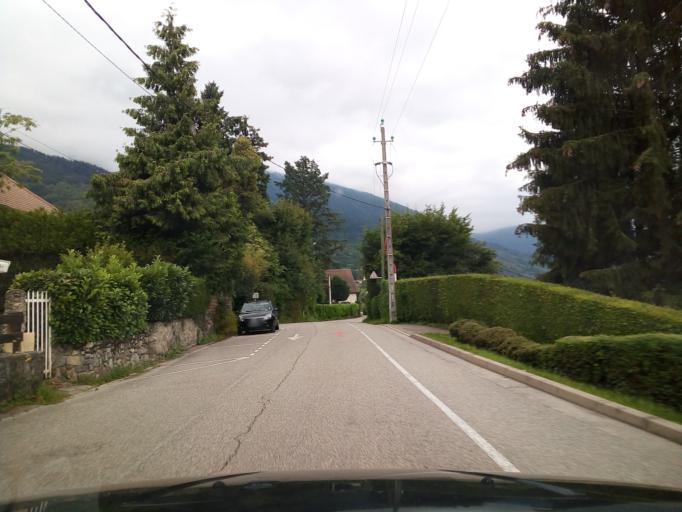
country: FR
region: Rhone-Alpes
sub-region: Departement de l'Isere
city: Vaulnaveys-le-Haut
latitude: 45.1453
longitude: 5.8392
